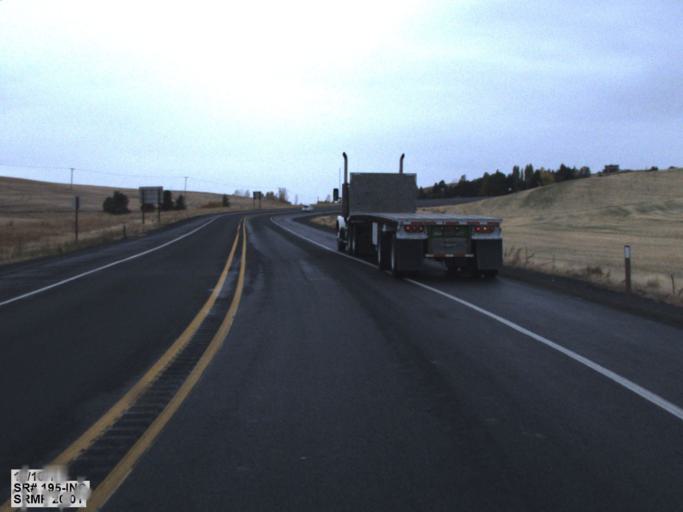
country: US
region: Washington
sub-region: Whitman County
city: Pullman
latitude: 46.7079
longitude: -117.2047
